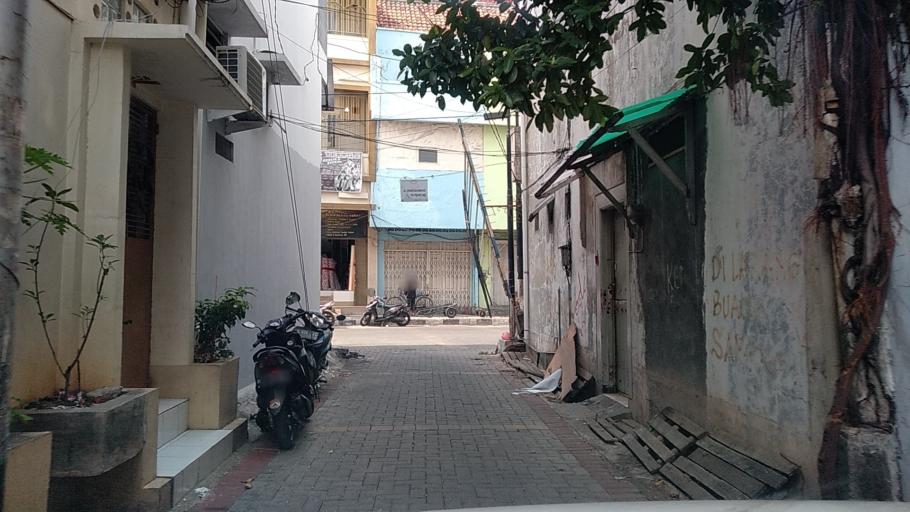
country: ID
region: Central Java
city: Semarang
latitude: -6.9748
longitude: 110.4262
